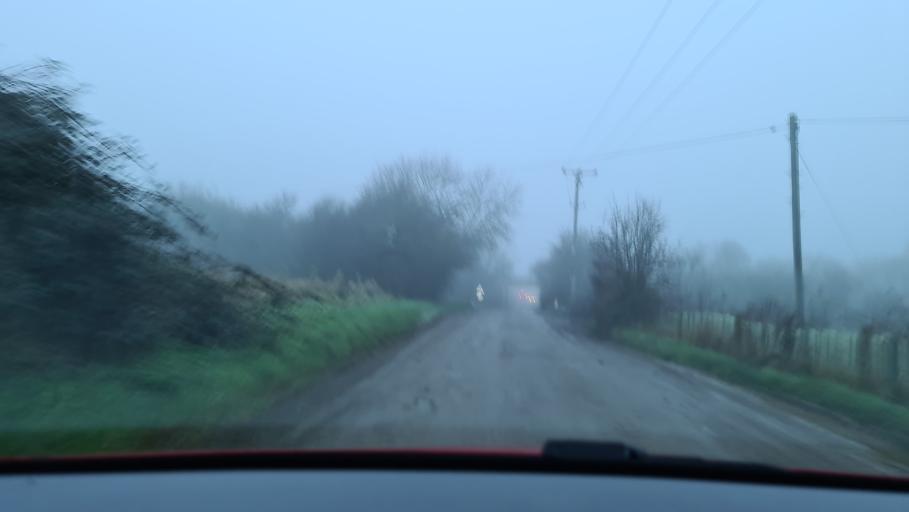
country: GB
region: England
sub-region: Buckinghamshire
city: Steeple Claydon
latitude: 51.8832
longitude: -0.9662
